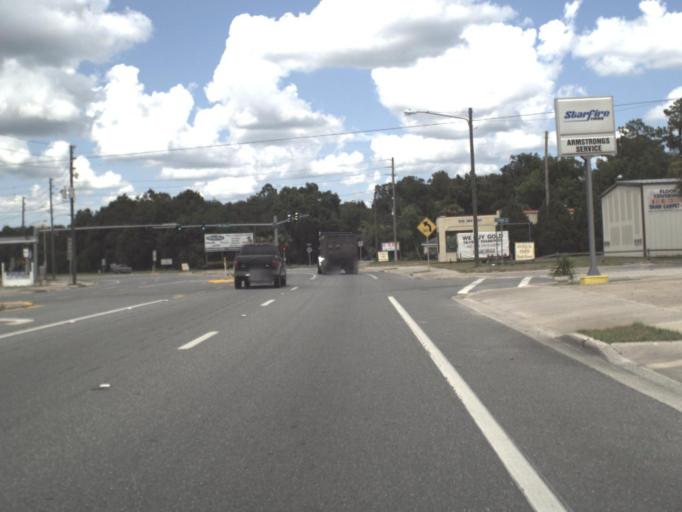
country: US
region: Florida
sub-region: Taylor County
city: Perry
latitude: 30.1168
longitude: -83.5892
